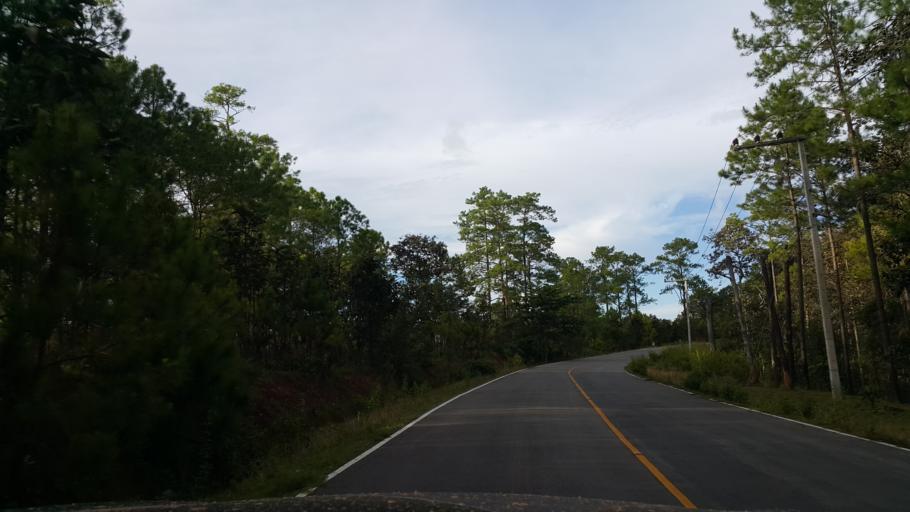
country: TH
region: Chiang Mai
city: Chaem Luang
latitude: 19.0911
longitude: 98.3404
